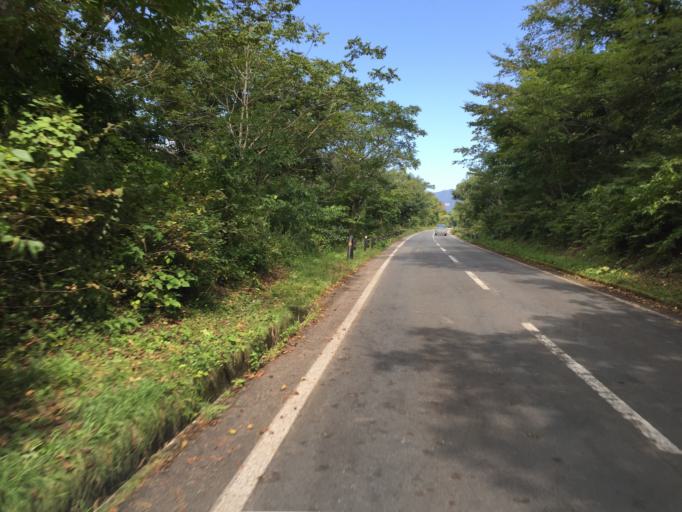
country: JP
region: Fukushima
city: Inawashiro
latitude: 37.6620
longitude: 140.0876
